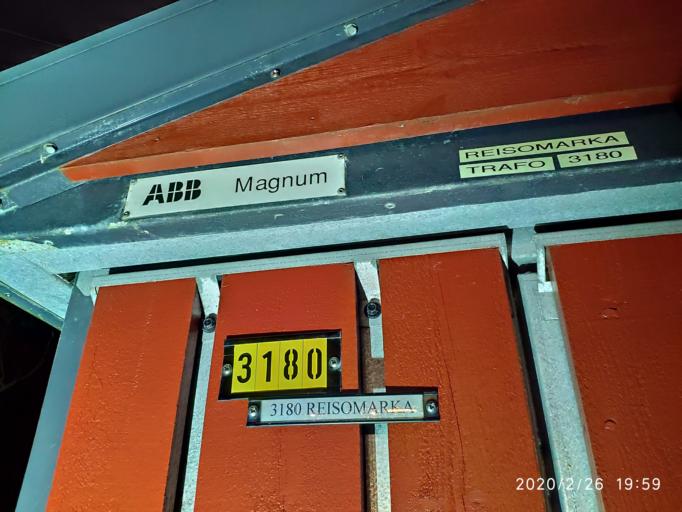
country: NO
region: Hordaland
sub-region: Tysnes
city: Uggdal
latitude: 60.0138
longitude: 5.5138
